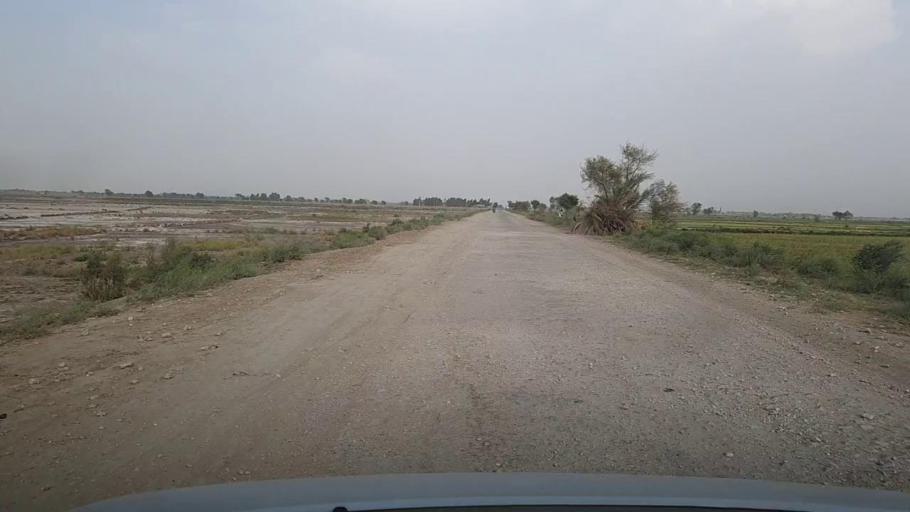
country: PK
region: Sindh
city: Dadu
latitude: 26.8148
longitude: 67.7718
